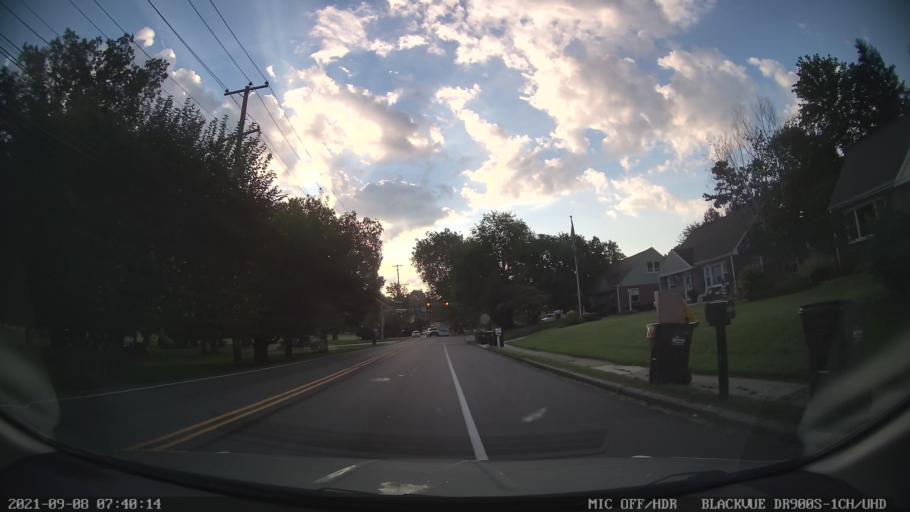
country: US
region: Pennsylvania
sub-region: Montgomery County
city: King of Prussia
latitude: 40.0815
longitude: -75.3765
